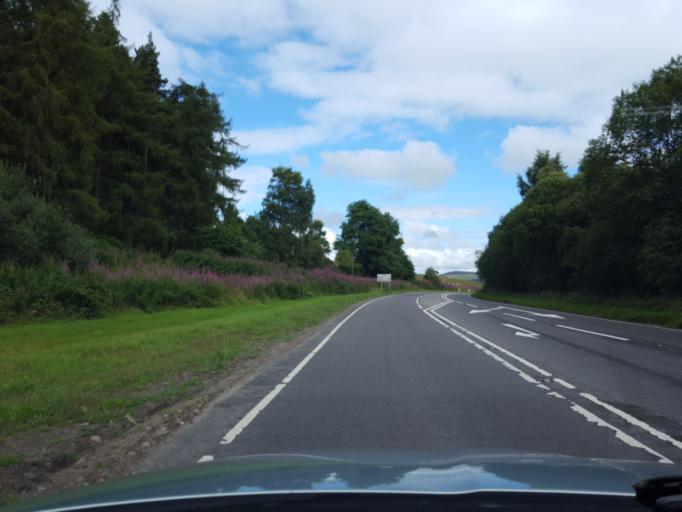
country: GB
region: Scotland
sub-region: Moray
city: Rothes
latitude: 57.4985
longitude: -3.1916
